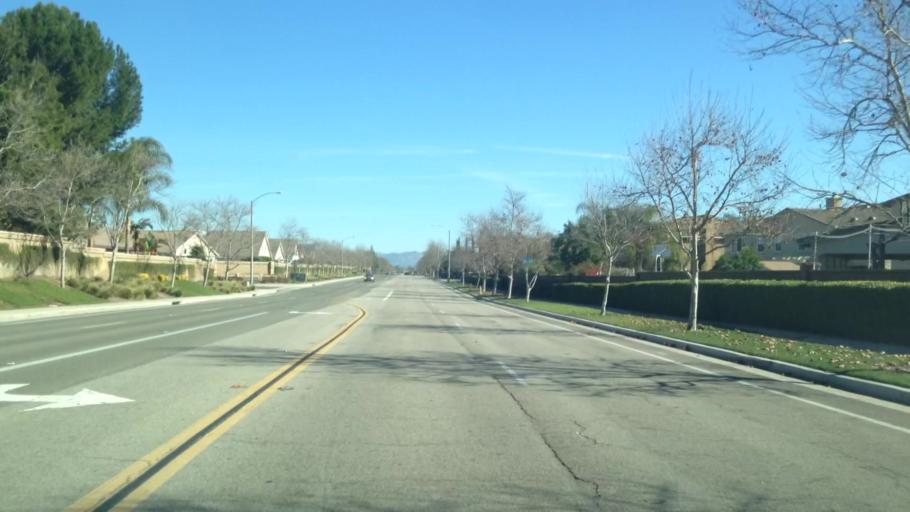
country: US
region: California
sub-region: Riverside County
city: Norco
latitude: 33.9681
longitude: -117.5841
